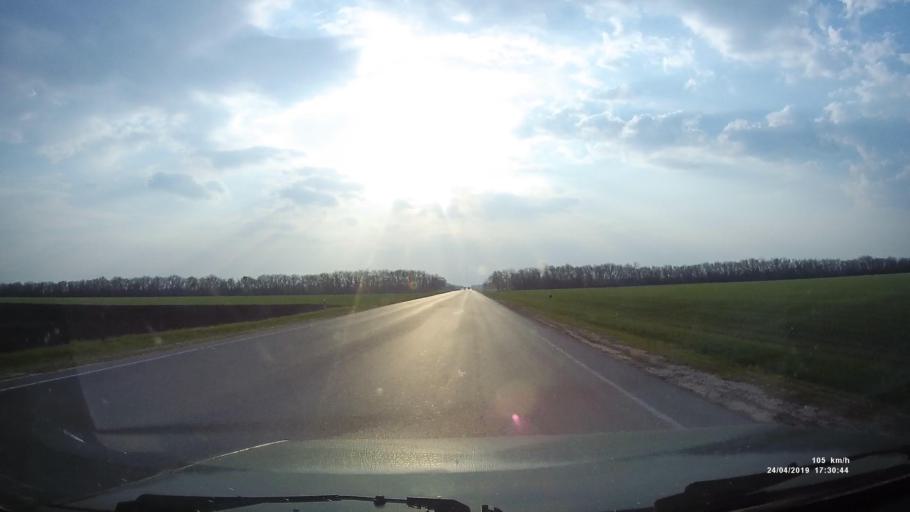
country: RU
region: Rostov
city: Tselina
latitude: 46.5224
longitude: 41.1355
